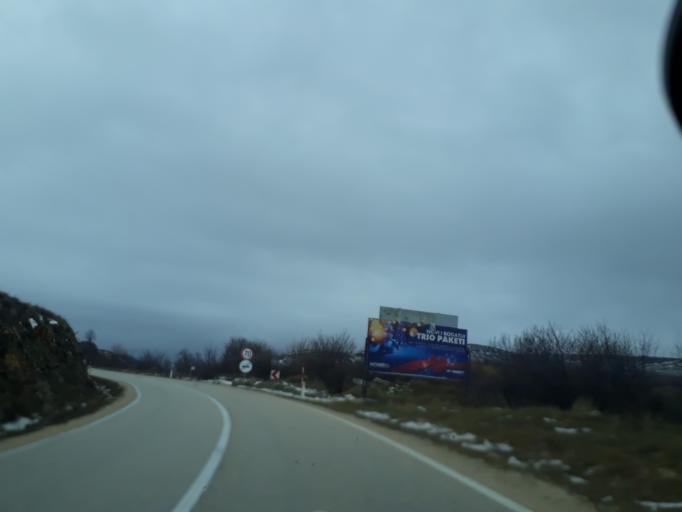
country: BA
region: Federation of Bosnia and Herzegovina
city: Tomislavgrad
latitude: 43.8214
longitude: 17.1932
